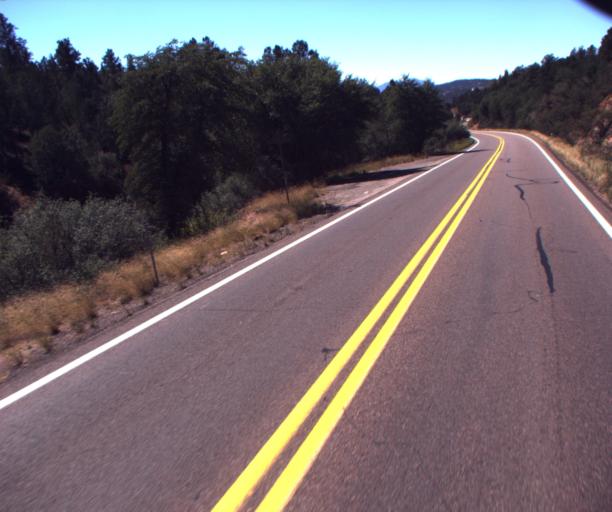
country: US
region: Arizona
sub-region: Gila County
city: Star Valley
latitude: 34.2622
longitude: -111.2459
